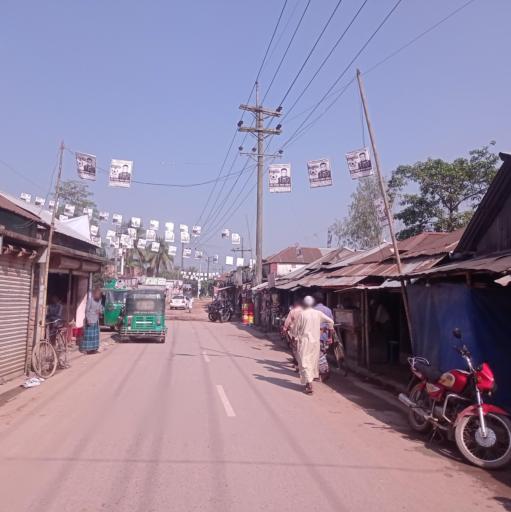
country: BD
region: Dhaka
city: Narsingdi
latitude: 24.0831
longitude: 90.6951
